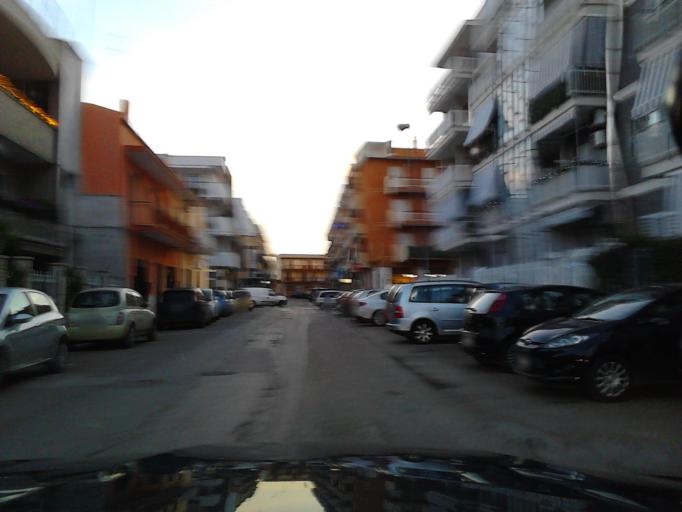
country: IT
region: Apulia
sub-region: Provincia di Bari
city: Valenzano
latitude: 41.0419
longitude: 16.8825
